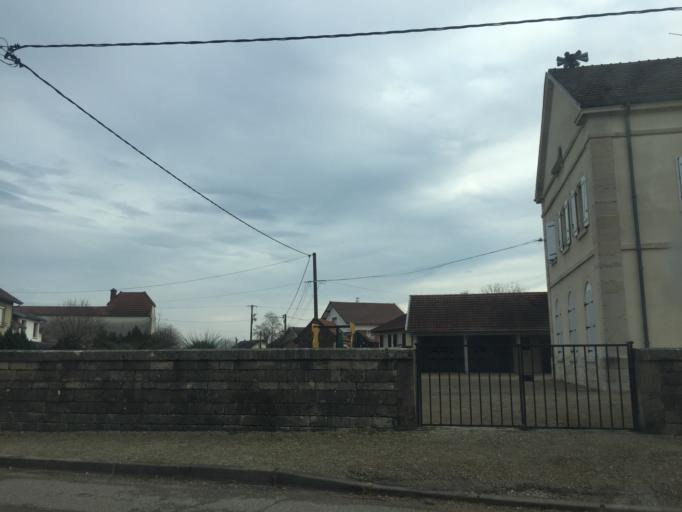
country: FR
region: Franche-Comte
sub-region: Departement du Jura
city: Tavaux
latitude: 47.0188
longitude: 5.4206
